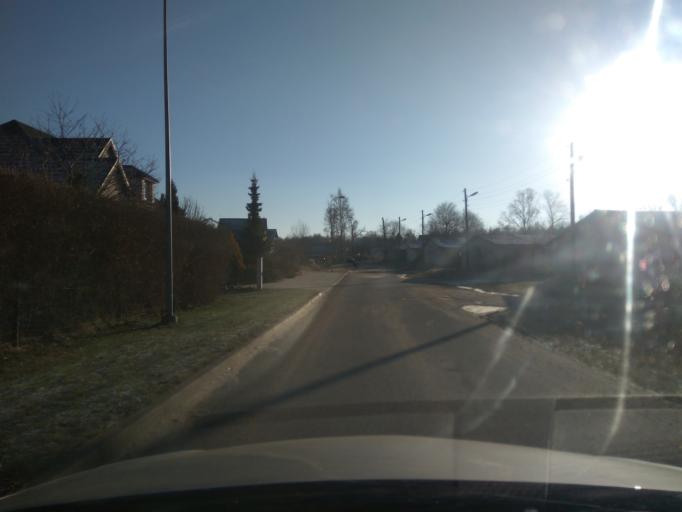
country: LV
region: Kuldigas Rajons
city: Kuldiga
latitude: 56.9673
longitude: 21.9416
